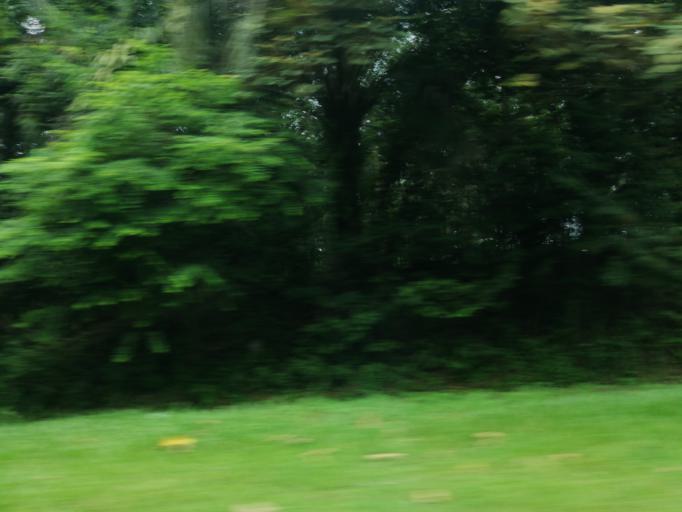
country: MY
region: Penang
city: Tasek Glugor
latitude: 5.4982
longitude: 100.6111
